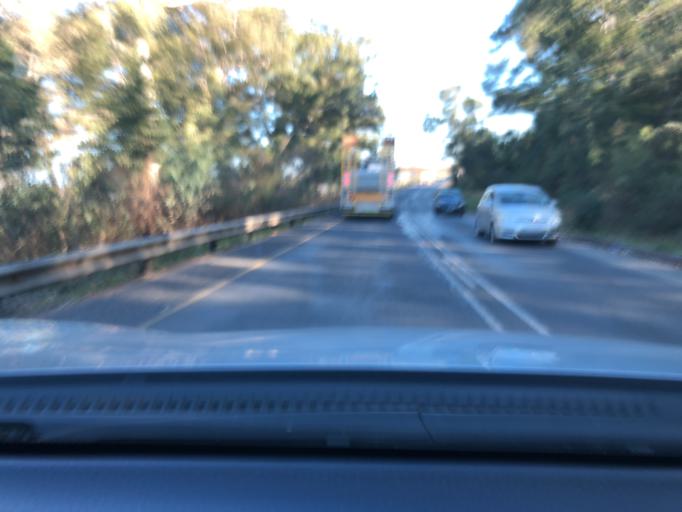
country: ZA
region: KwaZulu-Natal
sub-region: eThekwini Metropolitan Municipality
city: Umkomaas
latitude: -30.0271
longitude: 30.8124
